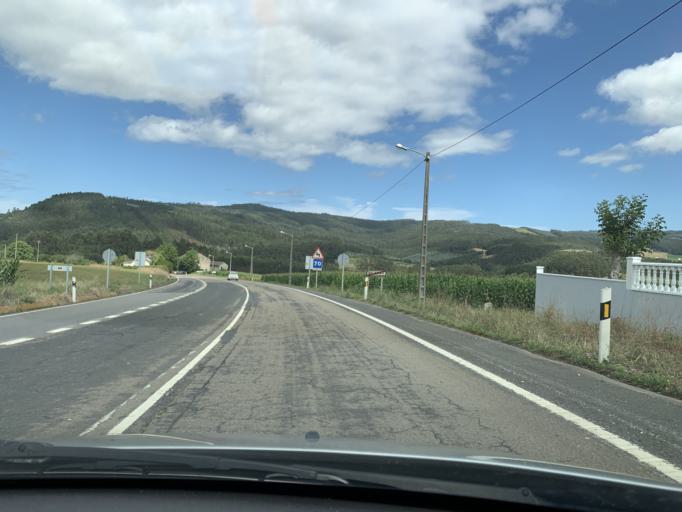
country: ES
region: Galicia
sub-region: Provincia de Lugo
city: Barreiros
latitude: 43.4984
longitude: -7.2706
